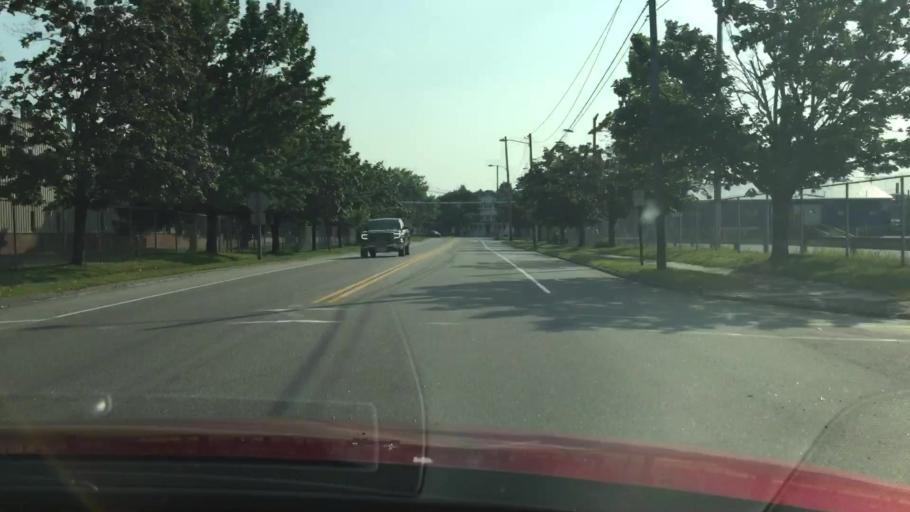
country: US
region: Maine
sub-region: Cumberland County
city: Westbrook
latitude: 43.6836
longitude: -70.3470
